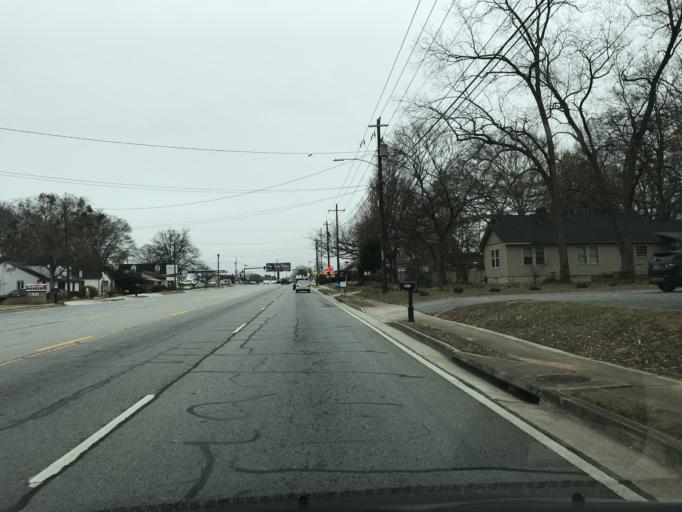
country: US
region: Georgia
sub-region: DeKalb County
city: Tucker
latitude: 33.8547
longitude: -84.2199
